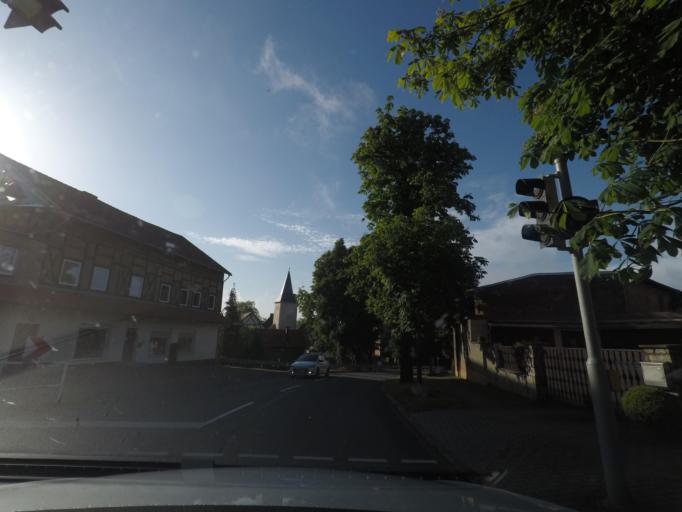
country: DE
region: Saxony-Anhalt
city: Huy-Neinstedt
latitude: 51.9388
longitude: 10.9096
